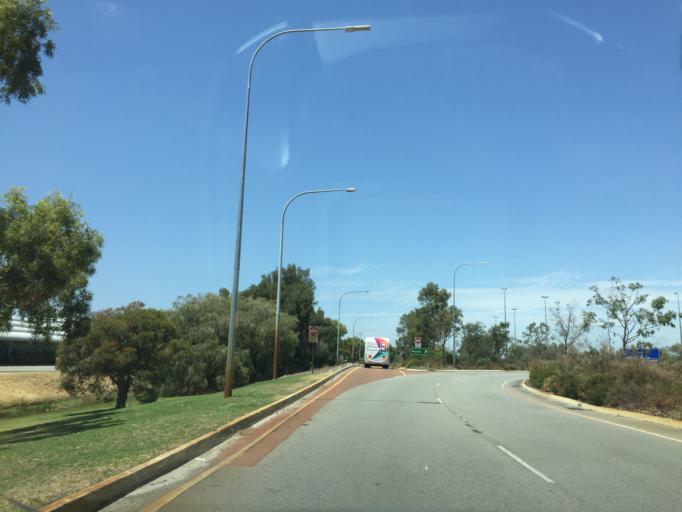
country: AU
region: Western Australia
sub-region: Belmont
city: Redcliffe
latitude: -31.9474
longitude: 115.9740
